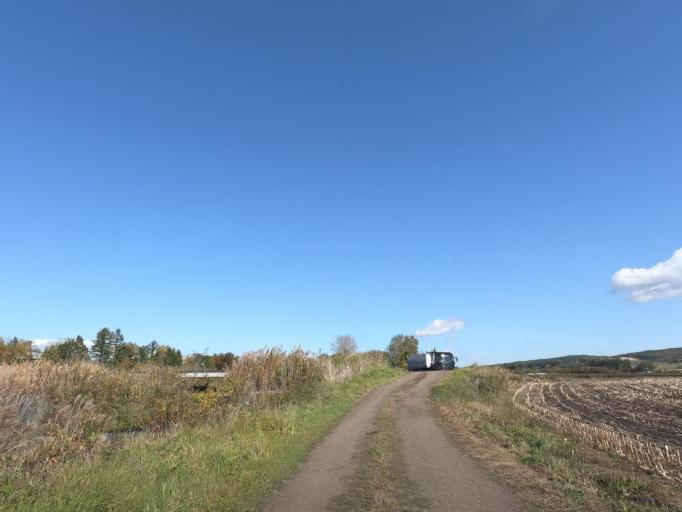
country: JP
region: Hokkaido
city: Otofuke
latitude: 43.0638
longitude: 143.2788
